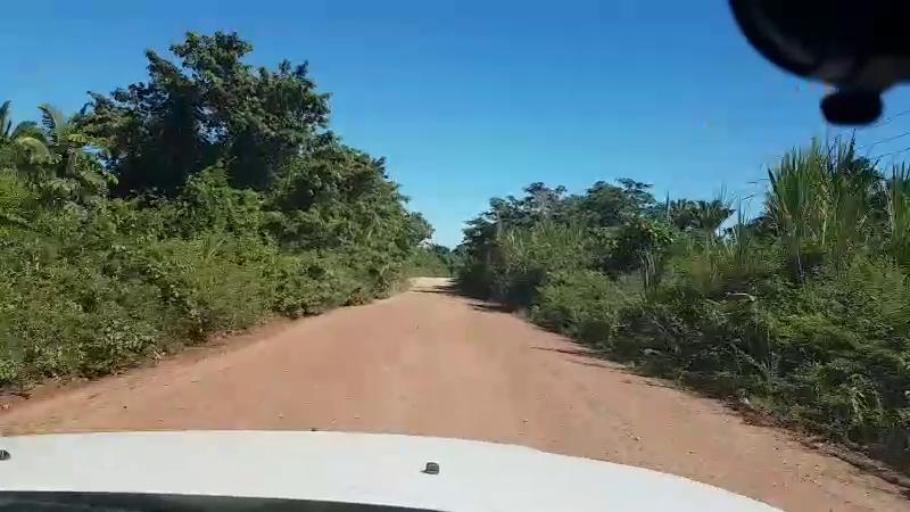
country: BZ
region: Stann Creek
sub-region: Dangriga
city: Dangriga
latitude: 17.1581
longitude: -88.3361
